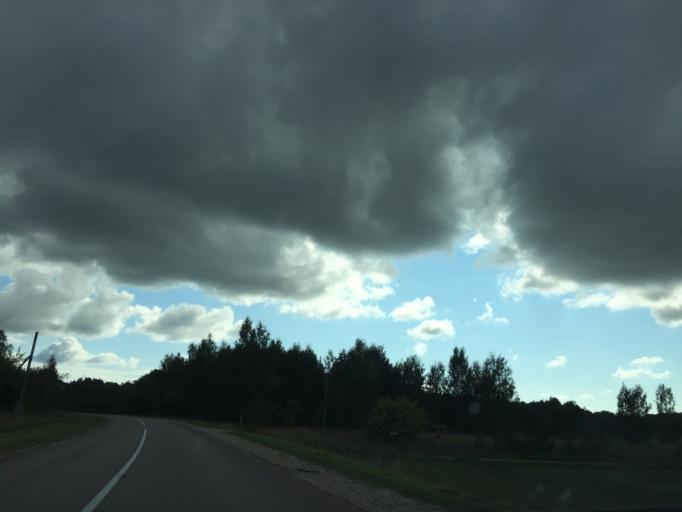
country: LV
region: Limbazu Rajons
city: Limbazi
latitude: 57.3668
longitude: 24.6728
